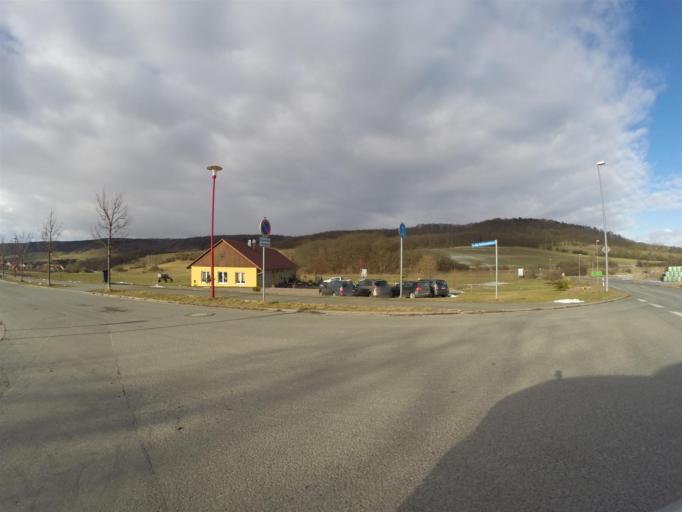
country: DE
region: Thuringia
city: Grosslobichau
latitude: 50.9261
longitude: 11.6910
